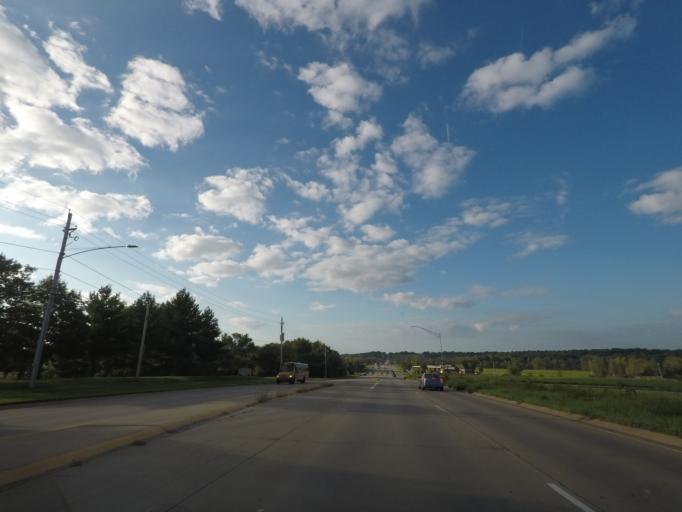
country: US
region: Iowa
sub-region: Warren County
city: Norwalk
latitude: 41.5146
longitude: -93.6451
